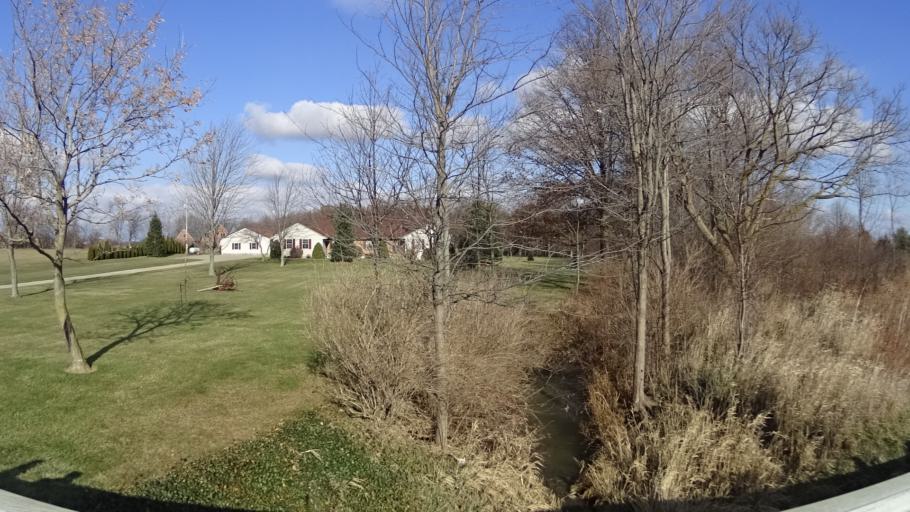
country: US
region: Ohio
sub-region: Lorain County
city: Camden
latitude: 41.2375
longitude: -82.2812
